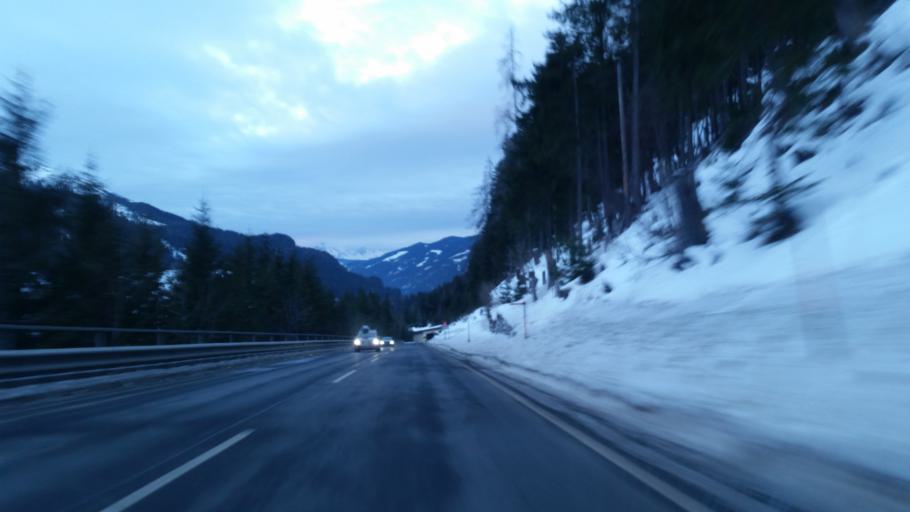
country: AT
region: Salzburg
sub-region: Politischer Bezirk Sankt Johann im Pongau
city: Untertauern
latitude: 47.2598
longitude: 13.4993
